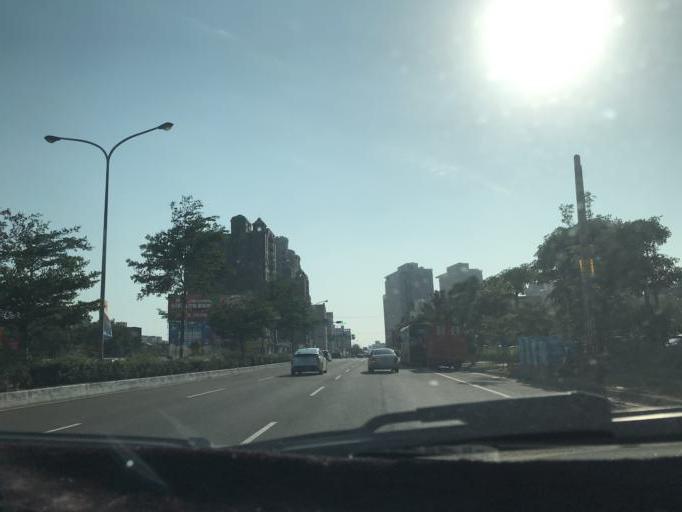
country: TW
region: Taiwan
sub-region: Hsinchu
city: Zhubei
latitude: 24.8248
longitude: 121.0322
